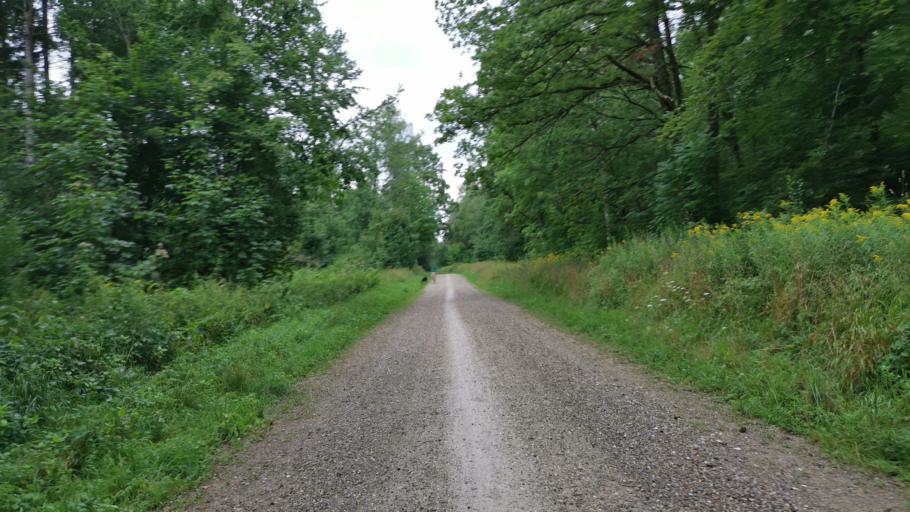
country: DE
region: Bavaria
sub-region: Upper Bavaria
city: Pullach im Isartal
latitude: 48.0761
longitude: 11.5552
